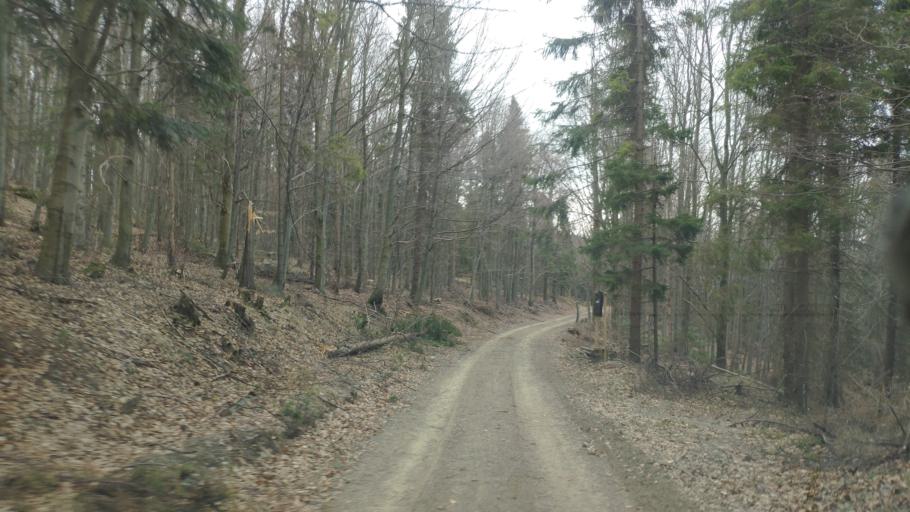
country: SK
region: Kosicky
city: Gelnica
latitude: 48.7541
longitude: 21.0408
